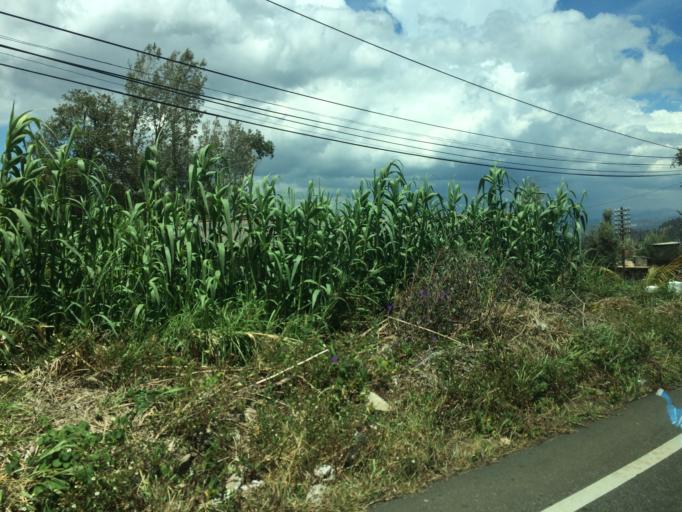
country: LK
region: Central
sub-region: Nuwara Eliya District
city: Nuwara Eliya
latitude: 6.9099
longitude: 80.8364
